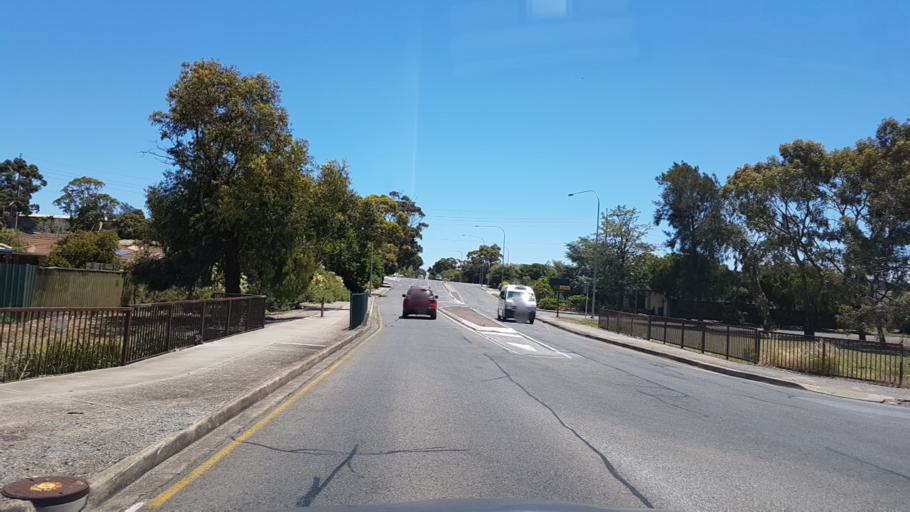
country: AU
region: South Australia
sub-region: Onkaparinga
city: Reynella
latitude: -35.0935
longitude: 138.5489
